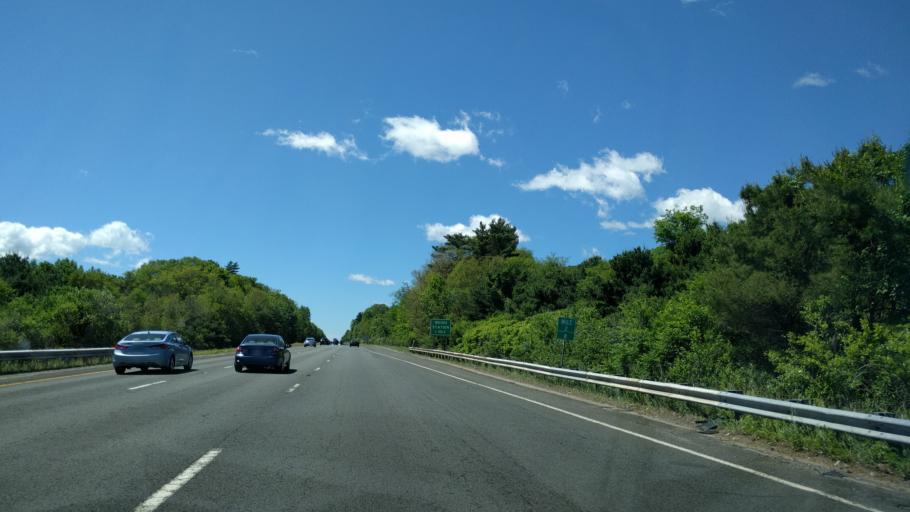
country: US
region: Massachusetts
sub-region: Hampden County
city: Holland
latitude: 42.0660
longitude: -72.1099
